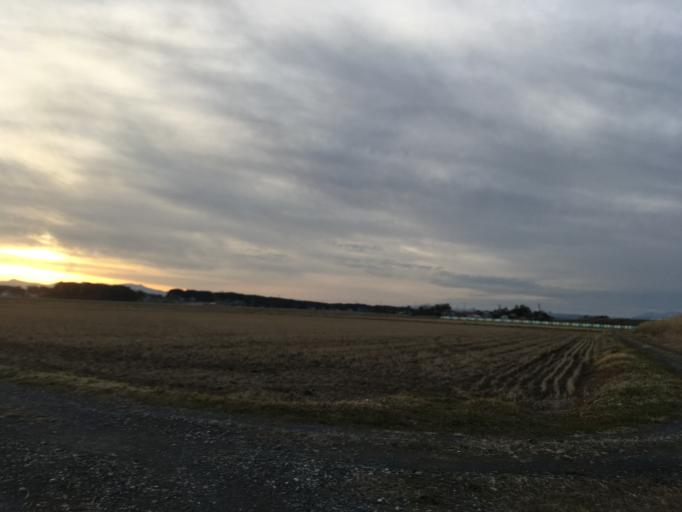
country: JP
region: Miyagi
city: Kogota
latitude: 38.6483
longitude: 141.0645
